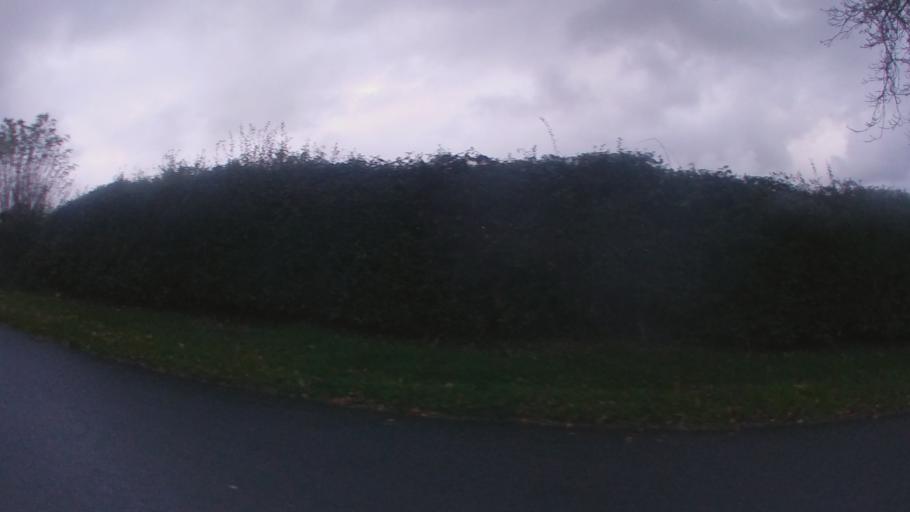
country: IE
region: Leinster
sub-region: Wicklow
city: Kilcoole
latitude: 53.1143
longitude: -6.0604
